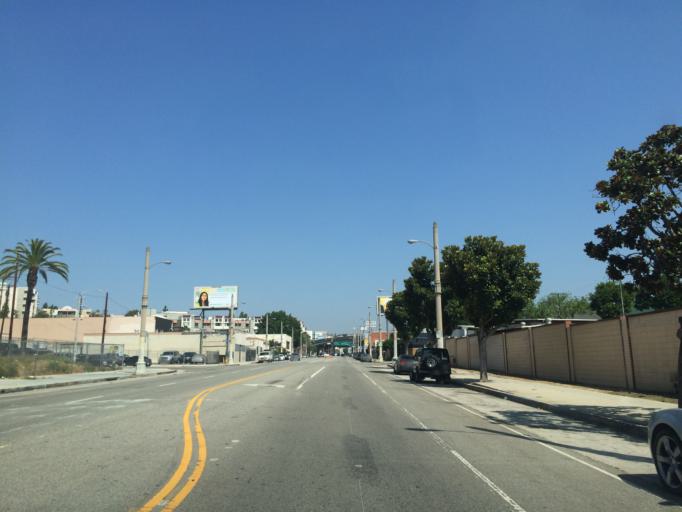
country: US
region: California
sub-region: Los Angeles County
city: Los Angeles
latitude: 34.0590
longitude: -118.2568
